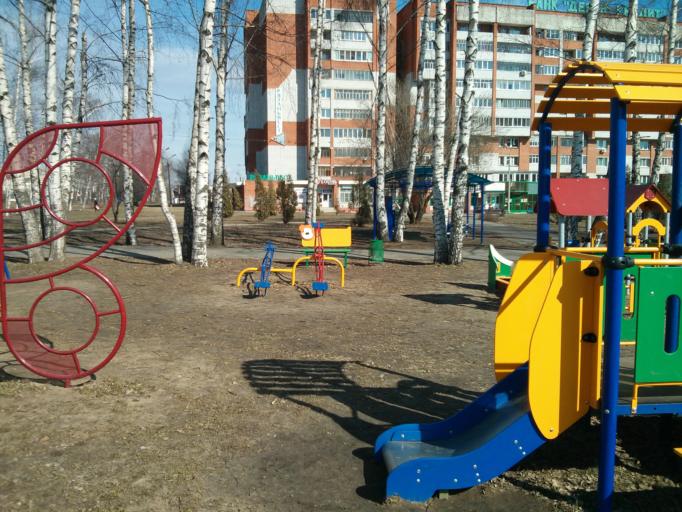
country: RU
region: Chuvashia
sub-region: Cheboksarskiy Rayon
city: Cheboksary
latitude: 56.1062
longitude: 47.2627
